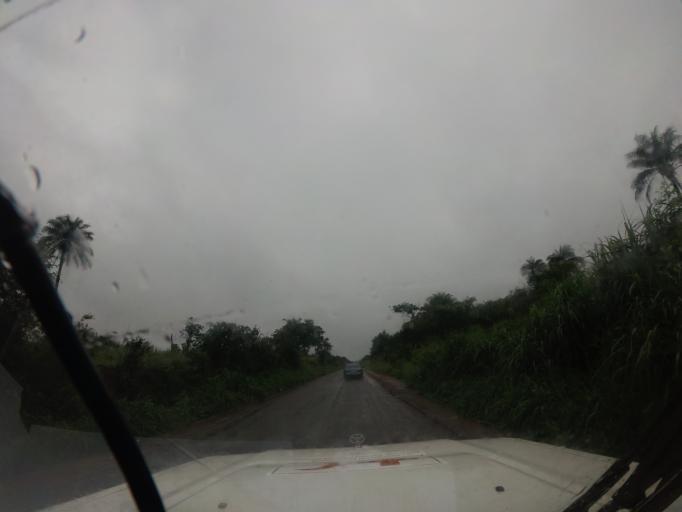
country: SL
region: Northern Province
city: Binkolo
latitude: 8.9360
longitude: -11.9951
